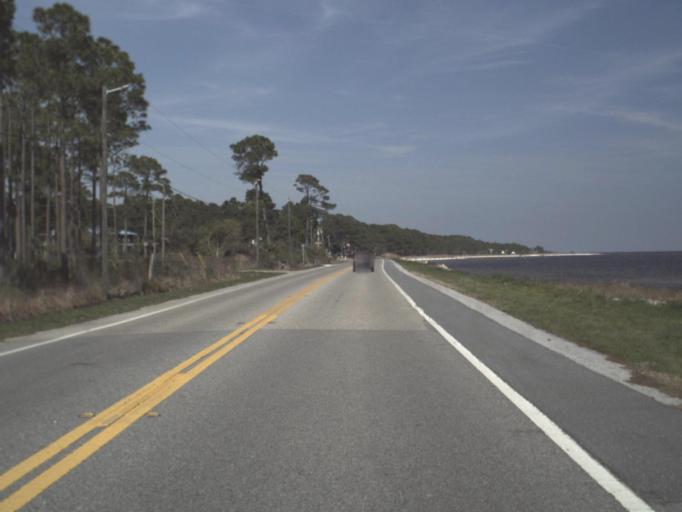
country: US
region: Florida
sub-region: Franklin County
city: Carrabelle
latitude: 29.8019
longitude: -84.7396
